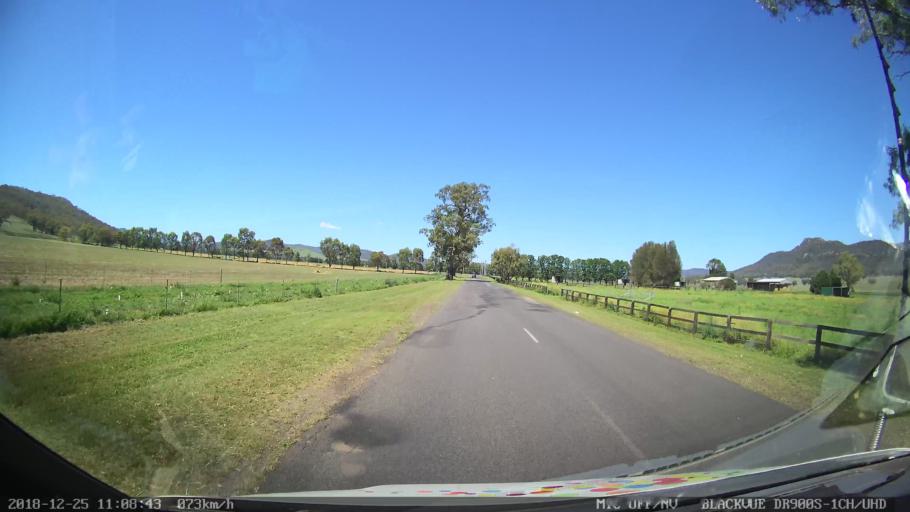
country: AU
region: New South Wales
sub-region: Upper Hunter Shire
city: Merriwa
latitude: -32.4044
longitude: 150.1226
